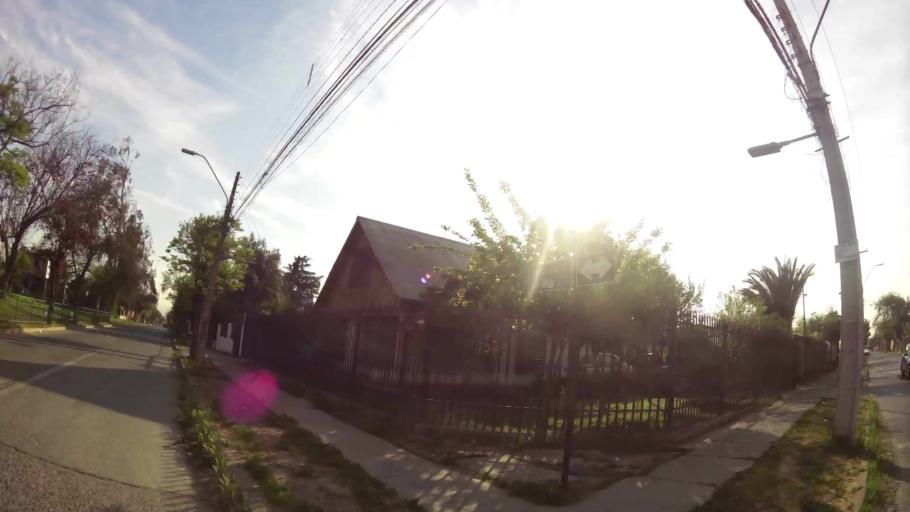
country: CL
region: Santiago Metropolitan
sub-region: Provincia de Santiago
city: Santiago
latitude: -33.5148
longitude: -70.6699
